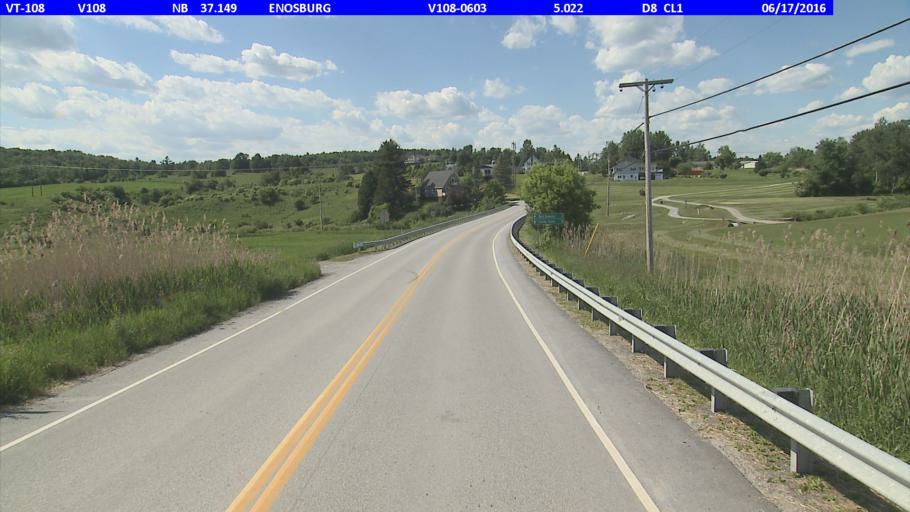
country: US
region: Vermont
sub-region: Franklin County
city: Enosburg Falls
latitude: 44.9129
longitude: -72.8042
